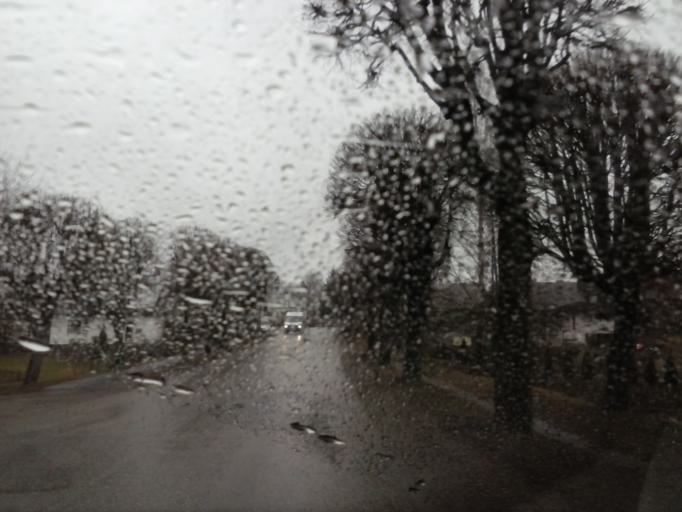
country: EE
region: Valgamaa
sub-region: Valga linn
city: Valga
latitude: 57.7819
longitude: 26.0349
